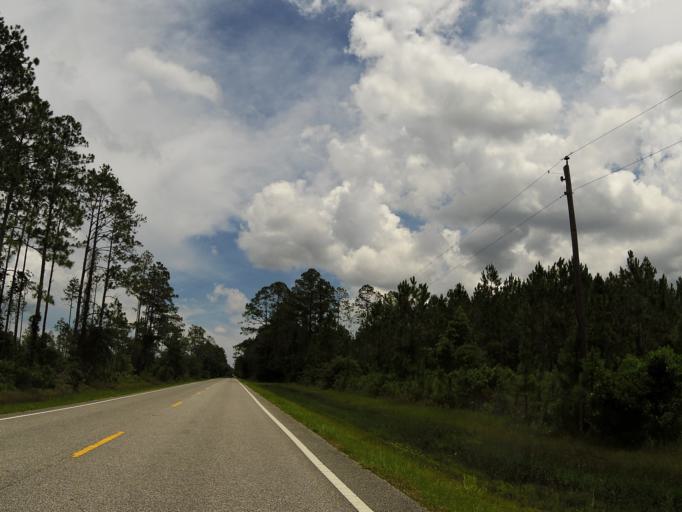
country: US
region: Florida
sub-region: Flagler County
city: Palm Coast
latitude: 29.6538
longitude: -81.3562
